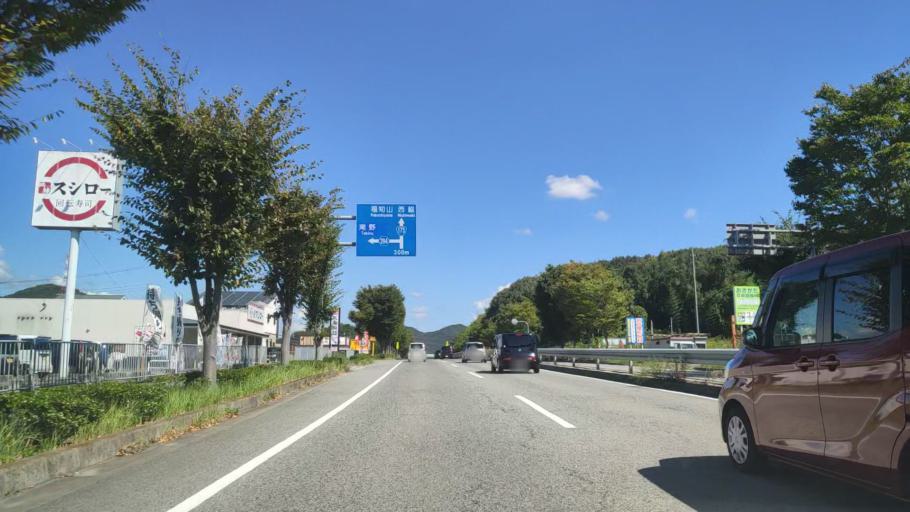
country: JP
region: Hyogo
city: Yashiro
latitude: 34.9425
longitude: 134.9671
